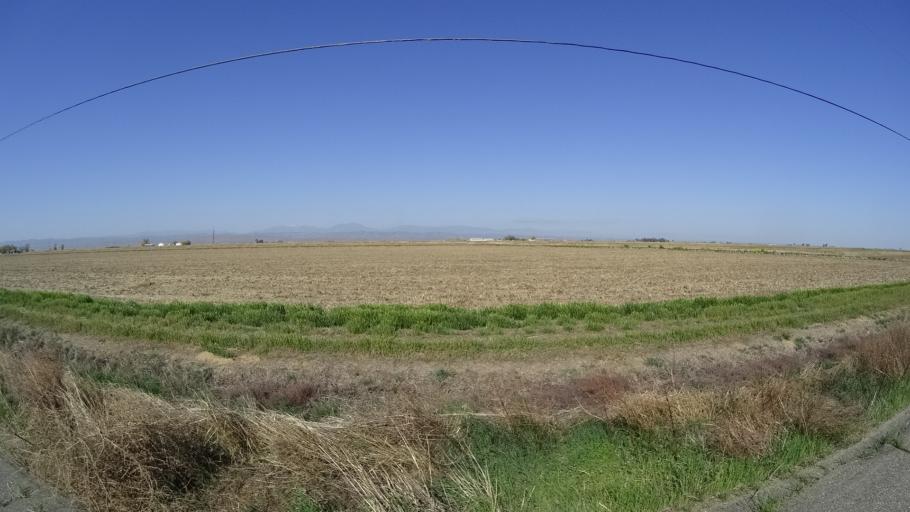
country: US
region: California
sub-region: Glenn County
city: Willows
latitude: 39.4100
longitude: -122.1960
